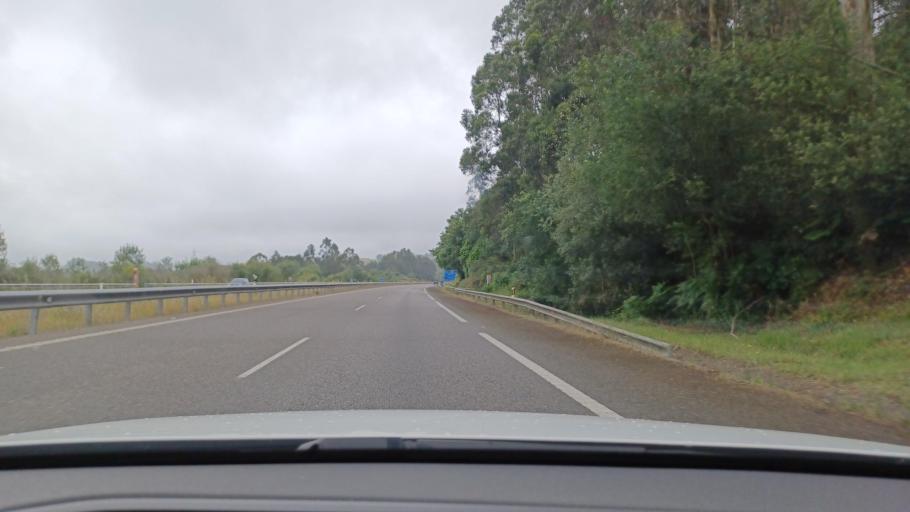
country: ES
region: Asturias
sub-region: Province of Asturias
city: Lugones
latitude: 43.4533
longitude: -5.7813
